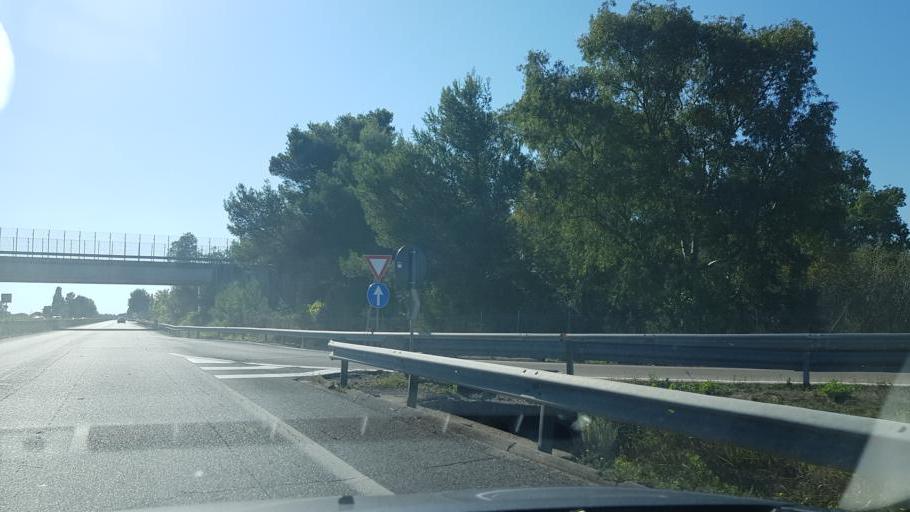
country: IT
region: Apulia
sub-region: Provincia di Brindisi
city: San Pietro Vernotico
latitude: 40.5216
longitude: 18.0163
